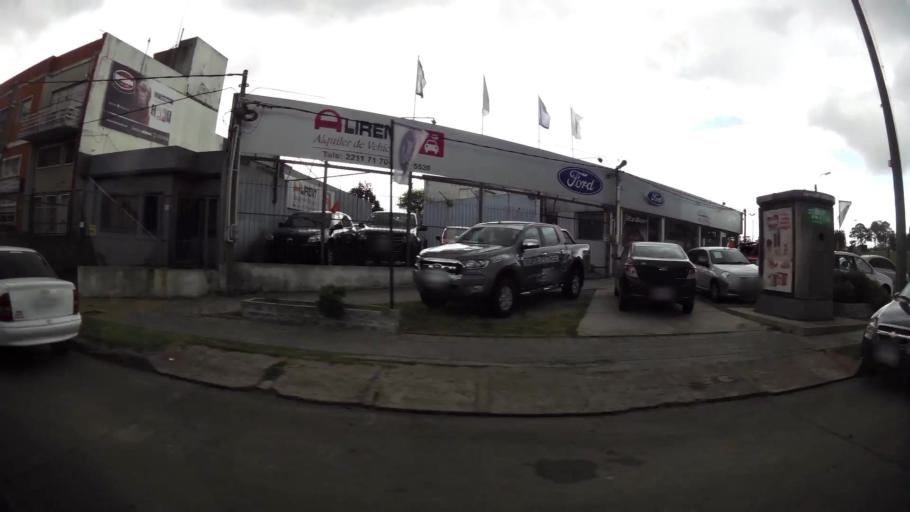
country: UY
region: Montevideo
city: Montevideo
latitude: -34.8668
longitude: -56.1641
